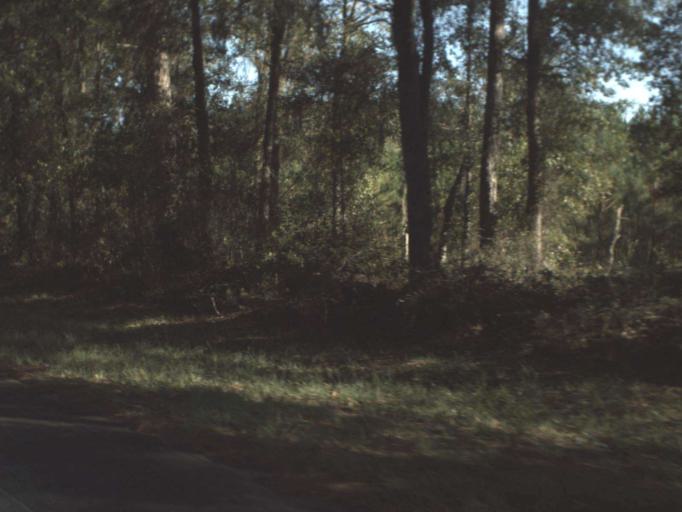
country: US
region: Georgia
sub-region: Brooks County
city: Quitman
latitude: 30.5884
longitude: -83.6398
